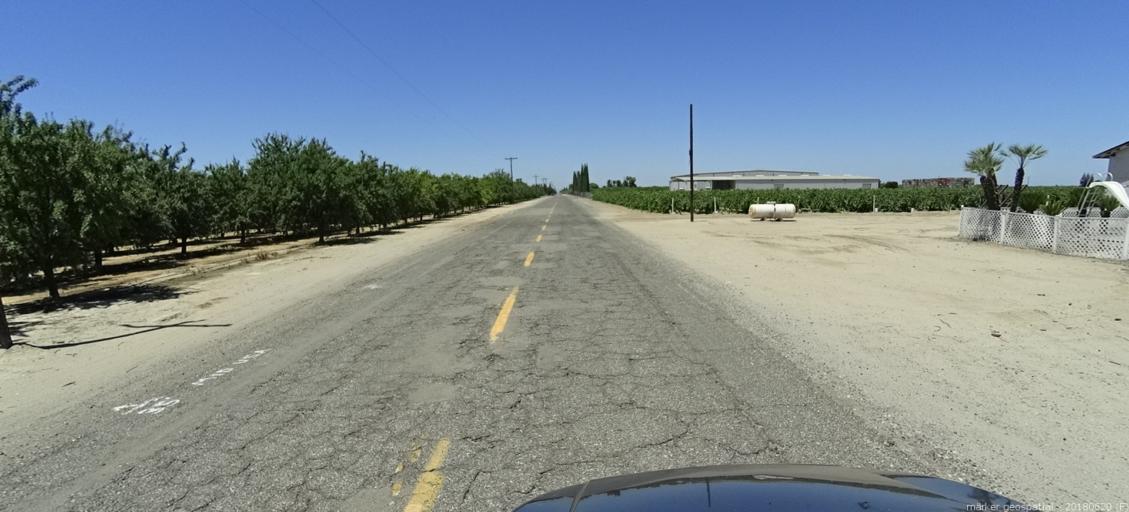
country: US
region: California
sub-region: Madera County
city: Parkwood
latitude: 36.8659
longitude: -120.0512
